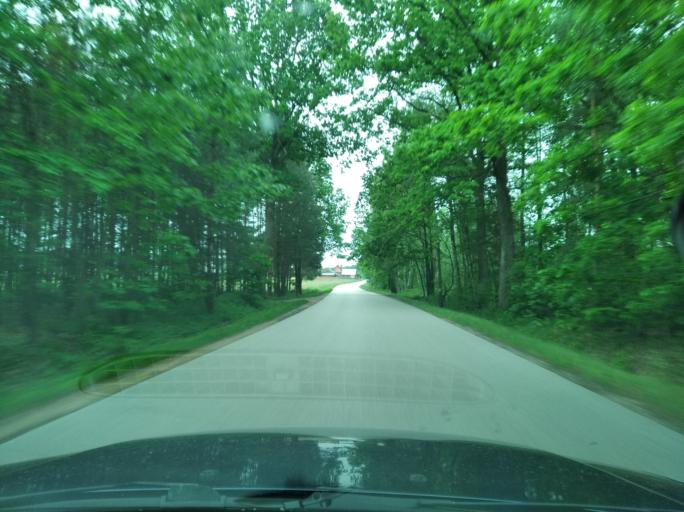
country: PL
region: Subcarpathian Voivodeship
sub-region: Powiat ropczycko-sedziszowski
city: Sedziszow Malopolski
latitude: 50.1258
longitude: 21.6718
